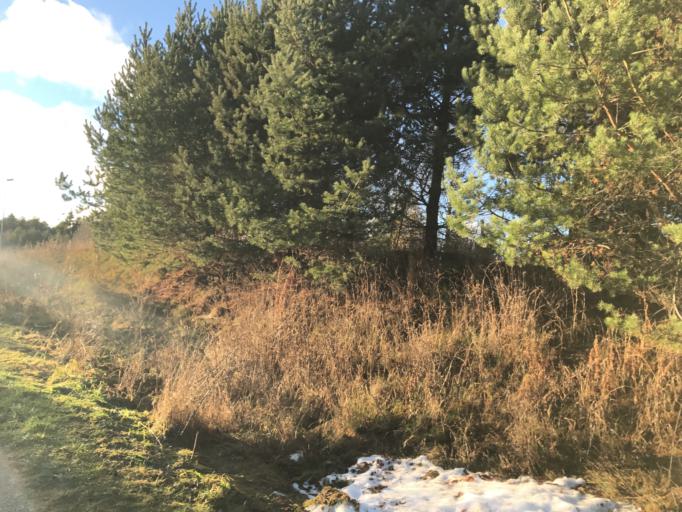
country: NO
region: Akershus
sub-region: Ullensaker
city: Jessheim
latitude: 60.1391
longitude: 11.1907
